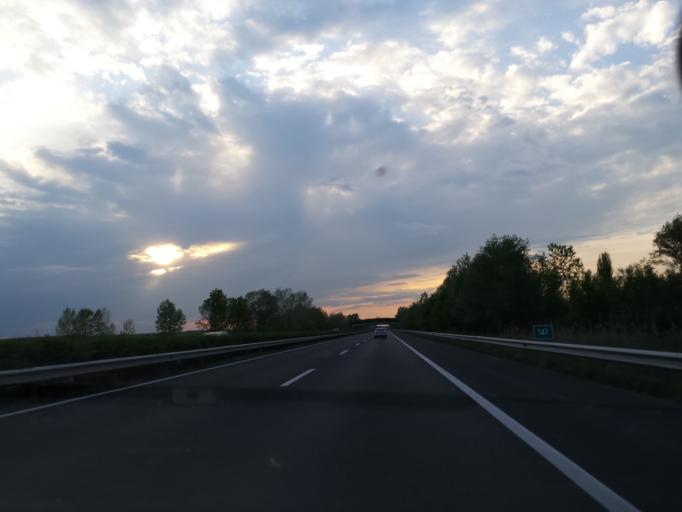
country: HU
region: Gyor-Moson-Sopron
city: Kimle
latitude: 47.7758
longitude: 17.3619
